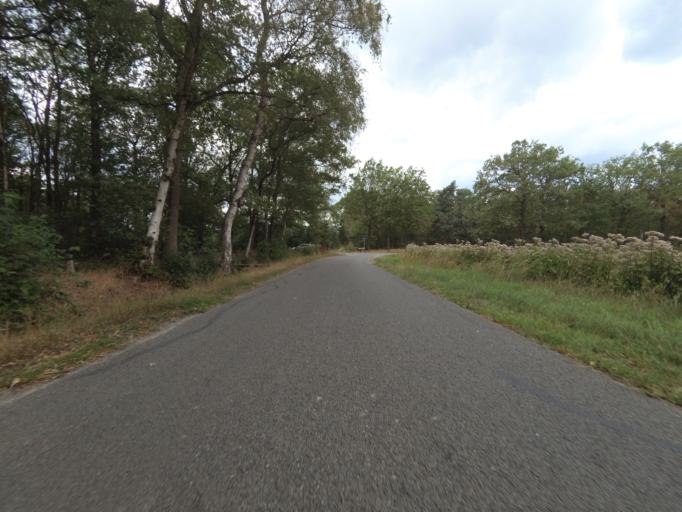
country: NL
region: Overijssel
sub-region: Gemeente Haaksbergen
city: Haaksbergen
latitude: 52.1413
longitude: 6.7825
